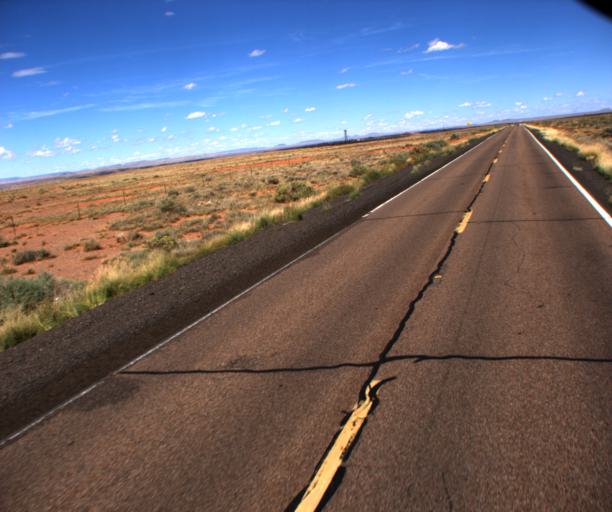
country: US
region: Arizona
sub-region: Navajo County
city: Holbrook
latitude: 34.8221
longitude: -110.1944
